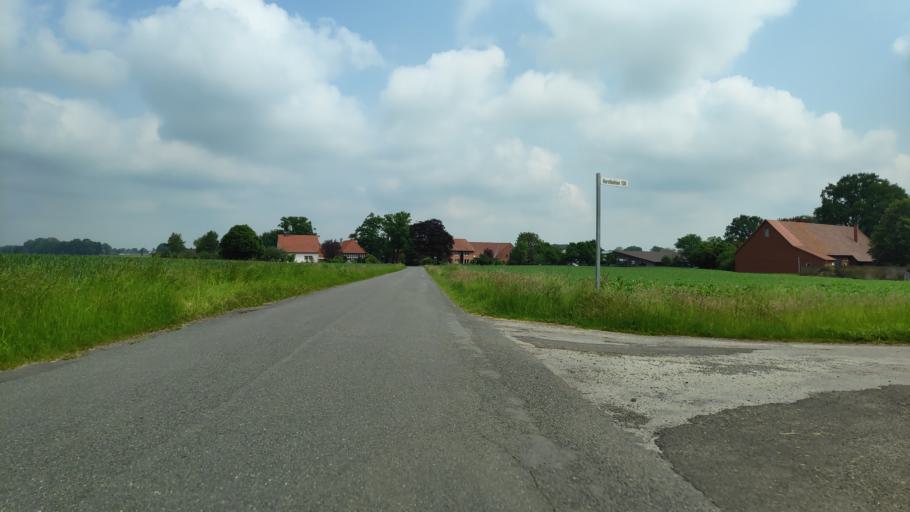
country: DE
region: North Rhine-Westphalia
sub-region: Regierungsbezirk Detmold
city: Hille
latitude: 52.3495
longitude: 8.7625
